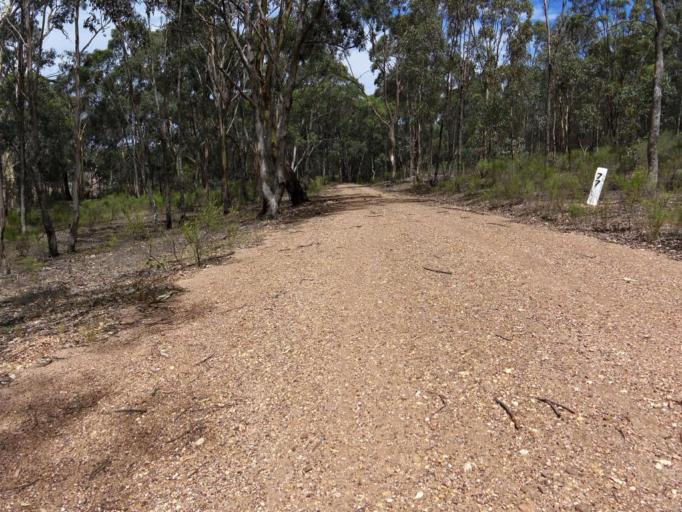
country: AU
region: Victoria
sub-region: Greater Bendigo
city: Kennington
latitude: -36.8862
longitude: 144.6570
